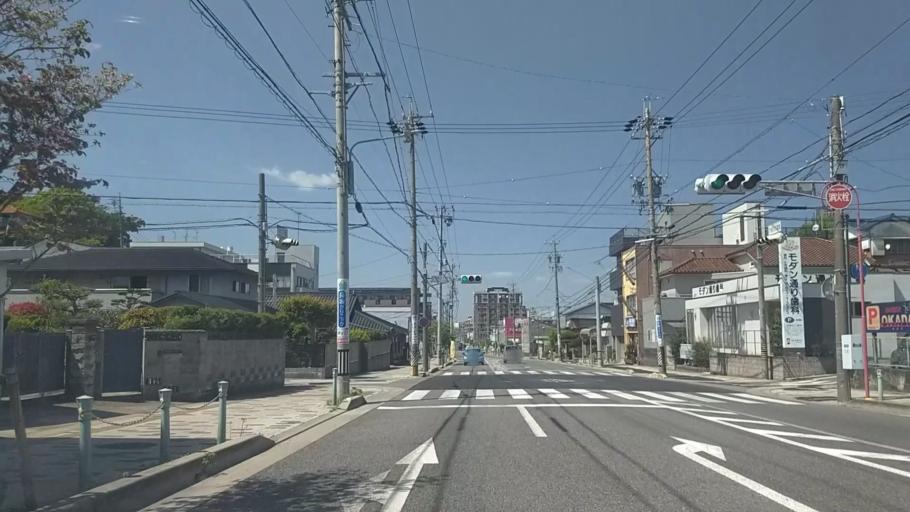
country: JP
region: Aichi
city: Okazaki
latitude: 34.9667
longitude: 137.1718
